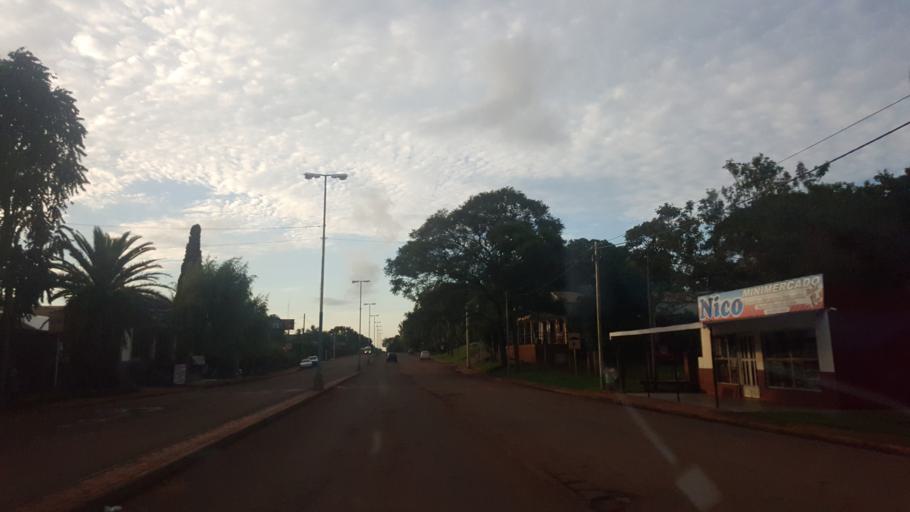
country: AR
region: Misiones
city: Dos de Mayo
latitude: -27.0206
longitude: -54.6873
